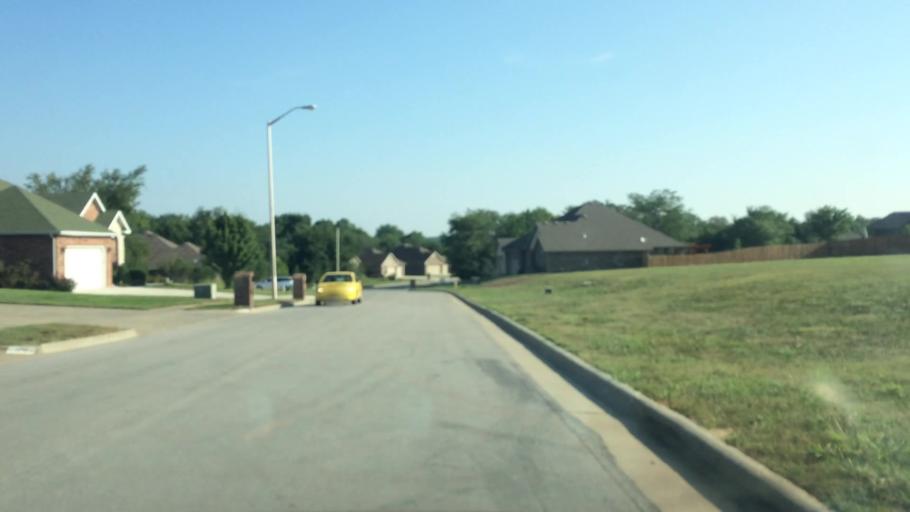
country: US
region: Missouri
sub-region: Greene County
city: Springfield
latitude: 37.2668
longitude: -93.2767
